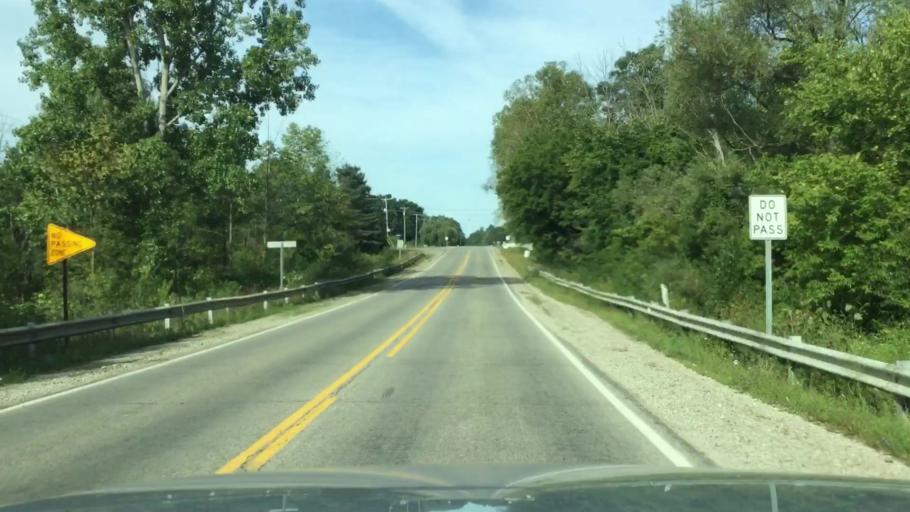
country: US
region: Michigan
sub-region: Genesee County
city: Flushing
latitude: 43.1179
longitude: -83.8265
